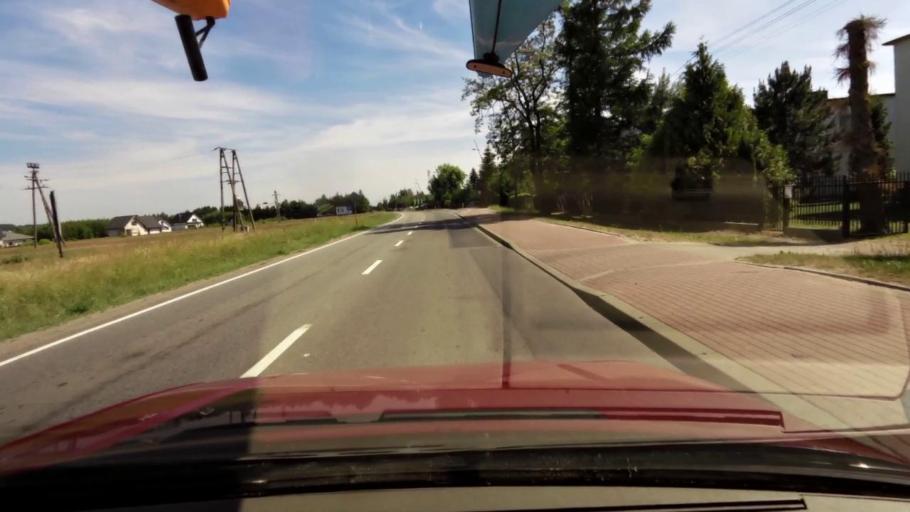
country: PL
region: Pomeranian Voivodeship
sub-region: Powiat slupski
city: Kobylnica
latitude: 54.4350
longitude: 16.9993
